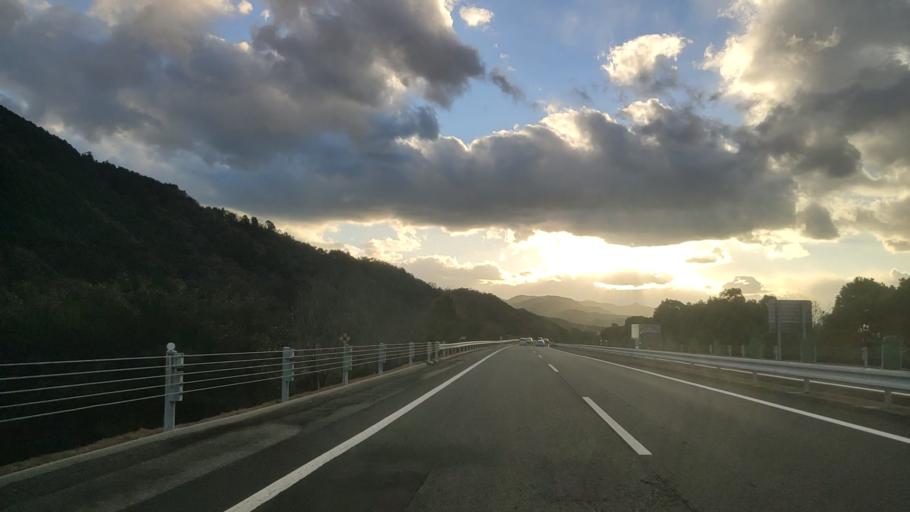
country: JP
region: Ehime
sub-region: Shikoku-chuo Shi
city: Matsuyama
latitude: 33.7915
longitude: 132.8972
